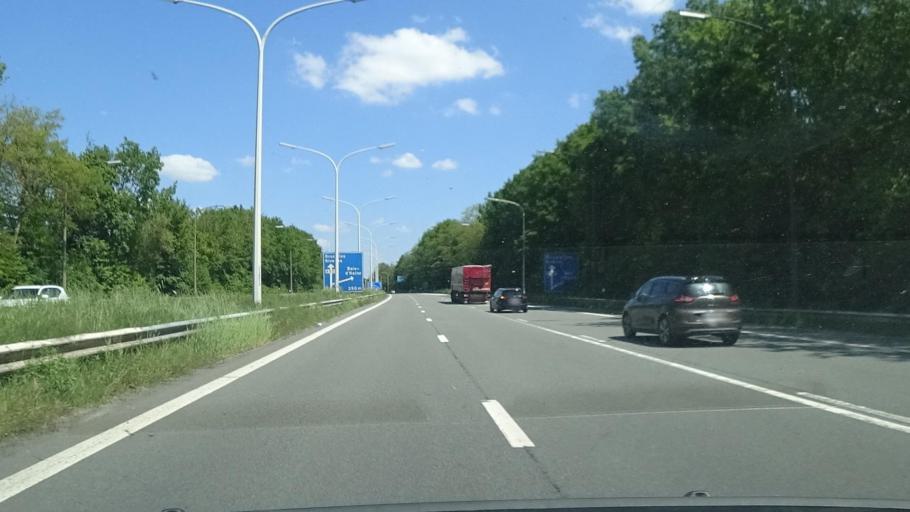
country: BE
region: Wallonia
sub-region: Province du Hainaut
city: Manage
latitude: 50.5026
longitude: 4.2117
